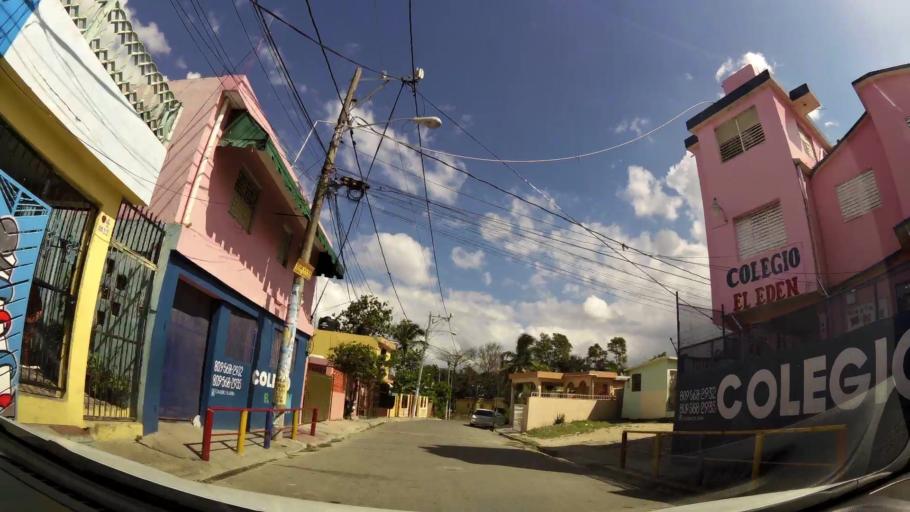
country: DO
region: Nacional
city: Ensanche Luperon
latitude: 18.5399
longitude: -69.9018
